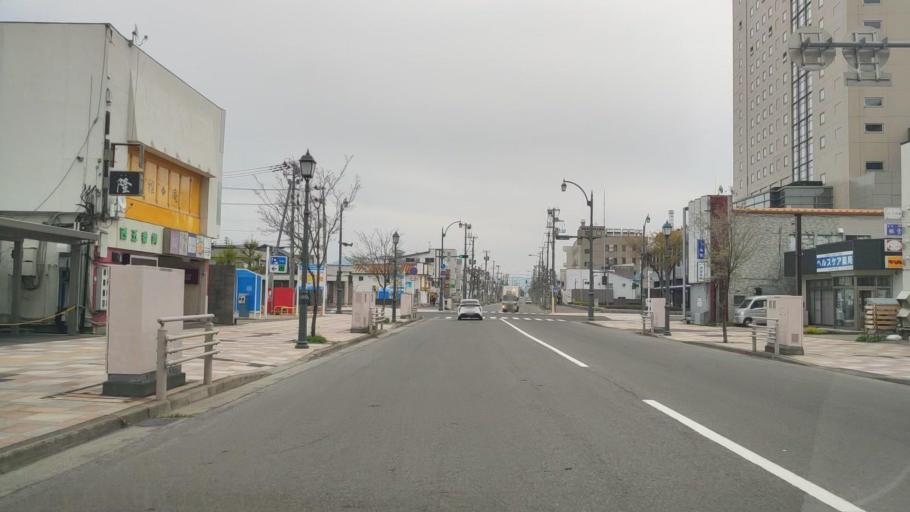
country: JP
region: Aomori
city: Aomori Shi
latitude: 40.8257
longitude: 140.7539
